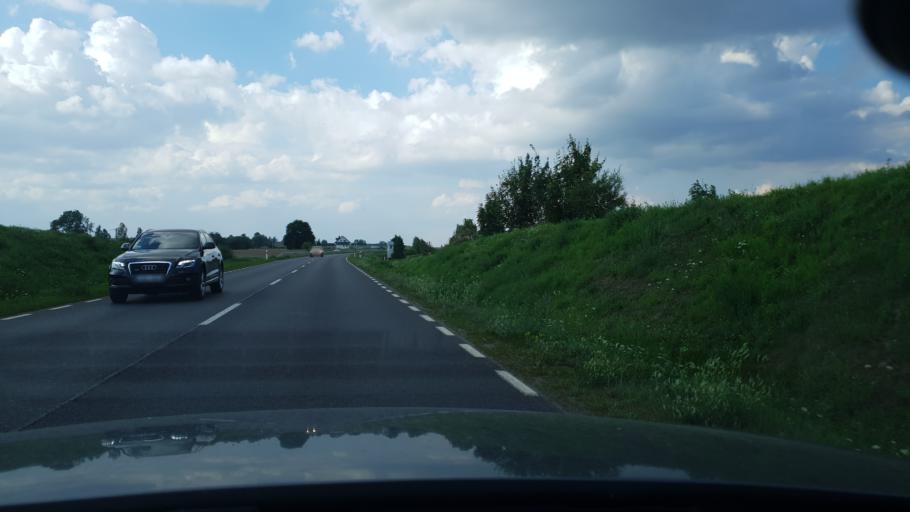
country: PL
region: Kujawsko-Pomorskie
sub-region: Powiat wabrzeski
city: Wabrzezno
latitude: 53.2916
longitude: 18.9263
